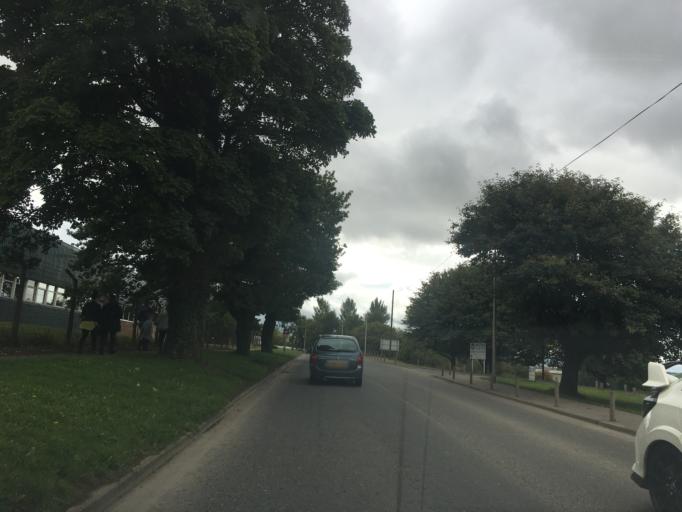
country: GB
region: Scotland
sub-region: Midlothian
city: Gorebridge
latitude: 55.8689
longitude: -3.0518
